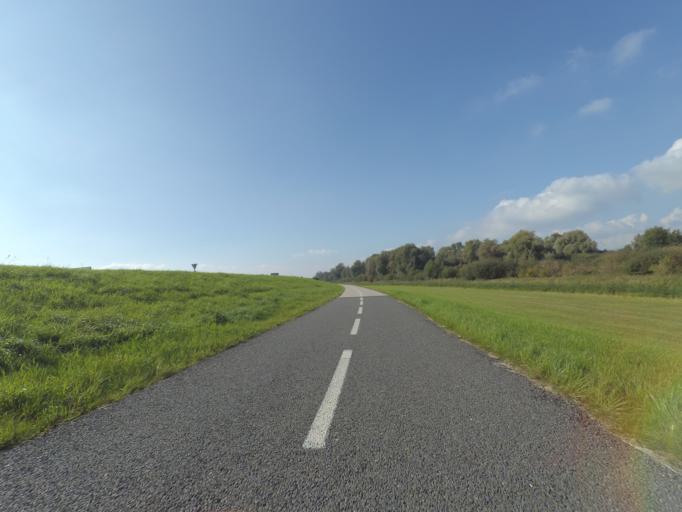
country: NL
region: Gelderland
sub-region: Gemeente Harderwijk
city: Harderwijk
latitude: 52.3667
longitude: 5.6061
